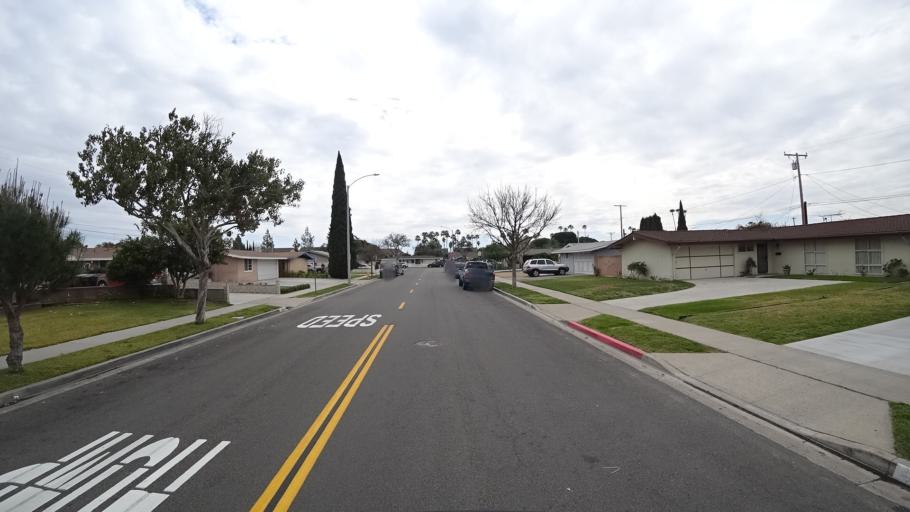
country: US
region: California
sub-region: Orange County
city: Anaheim
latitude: 33.8453
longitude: -117.9365
